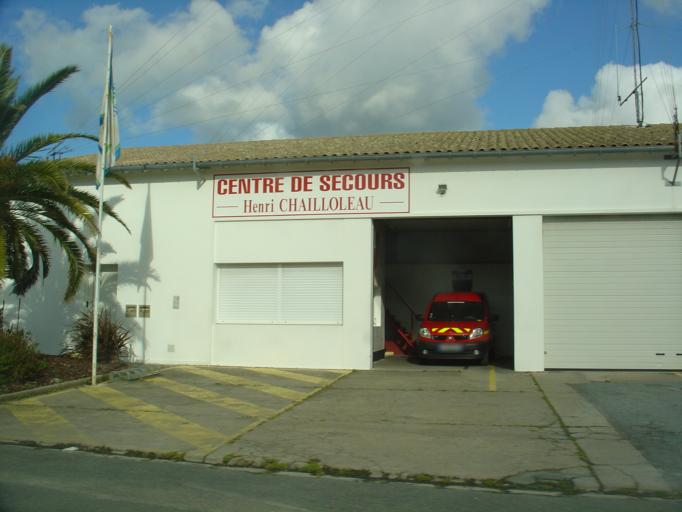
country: FR
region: Poitou-Charentes
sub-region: Departement de la Charente-Maritime
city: Dolus-d'Oleron
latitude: 45.9419
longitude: -1.3115
